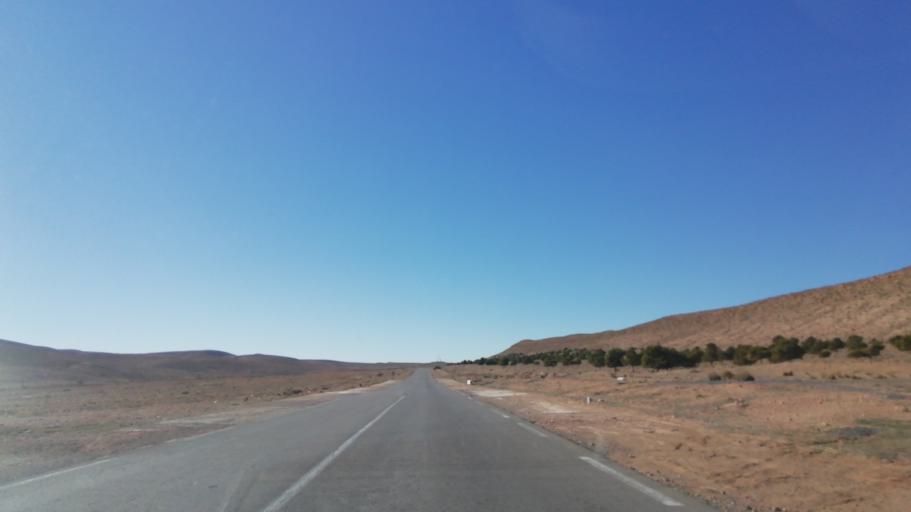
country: DZ
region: El Bayadh
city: El Bayadh
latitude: 33.6847
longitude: 1.4580
